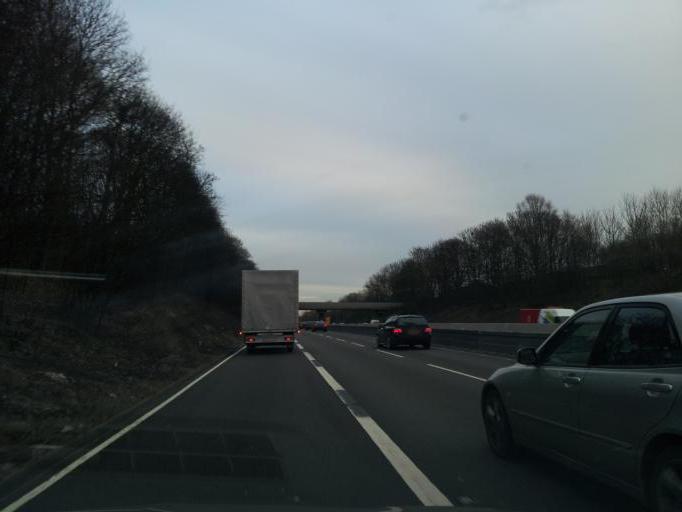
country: GB
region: England
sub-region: Northamptonshire
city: Bugbrooke
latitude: 52.2331
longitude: -1.0277
